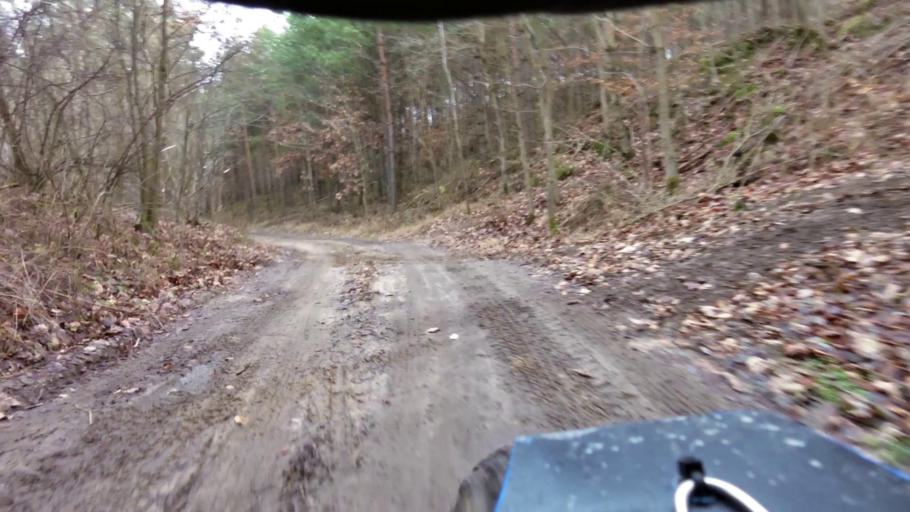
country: PL
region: Lubusz
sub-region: Powiat gorzowski
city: Jenin
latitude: 52.7181
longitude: 15.1269
